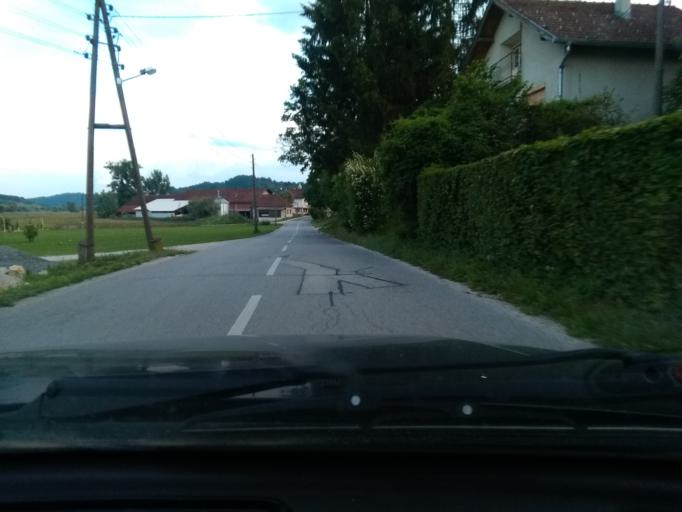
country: HR
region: Krapinsko-Zagorska
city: Pregrada
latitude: 46.0810
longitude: 15.7471
